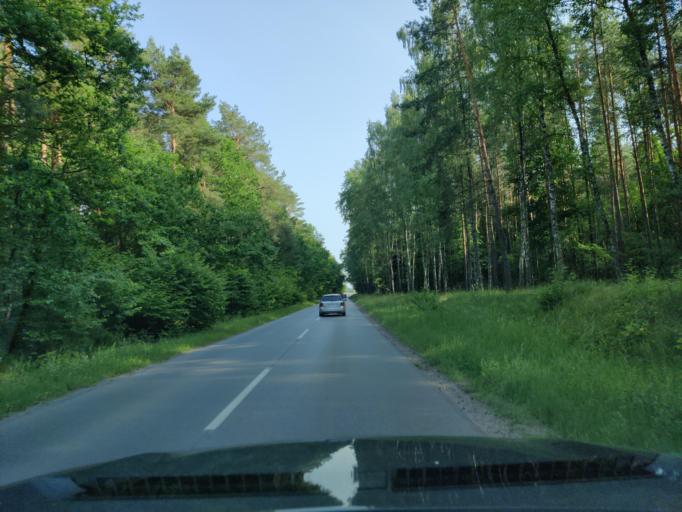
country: PL
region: Masovian Voivodeship
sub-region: Powiat wyszkowski
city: Wyszkow
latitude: 52.6252
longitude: 21.4517
